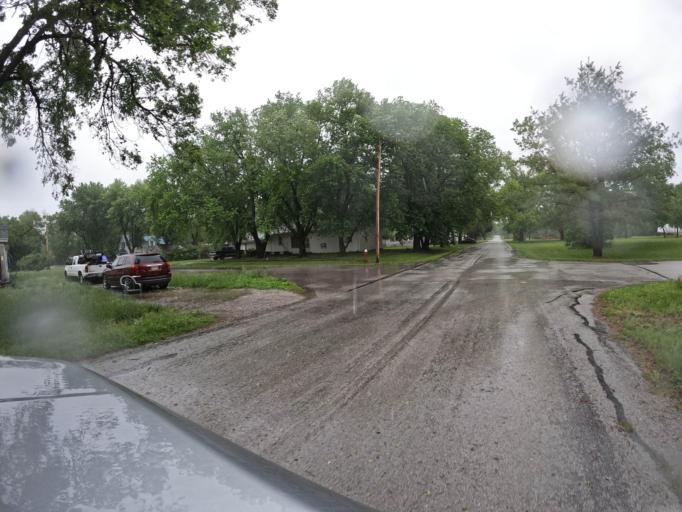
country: US
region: Nebraska
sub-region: Gage County
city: Wymore
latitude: 40.1412
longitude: -96.6670
